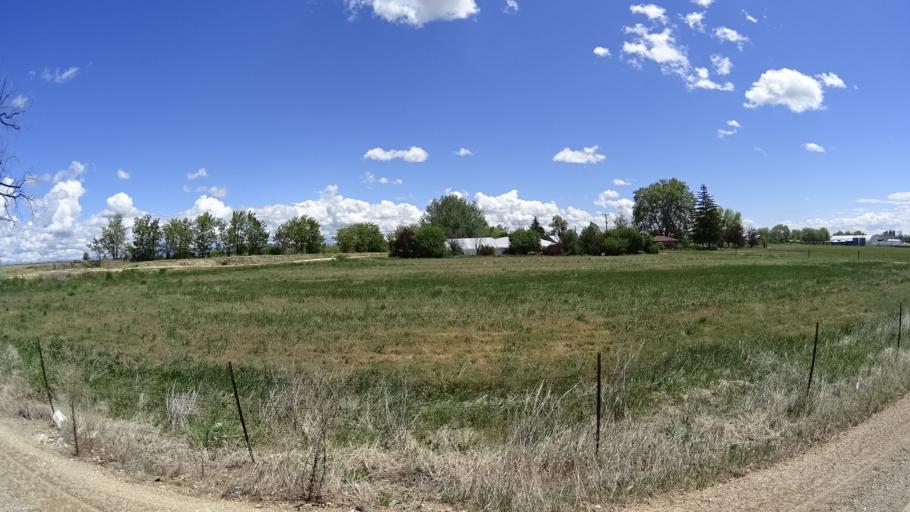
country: US
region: Idaho
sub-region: Ada County
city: Meridian
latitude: 43.5701
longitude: -116.4736
